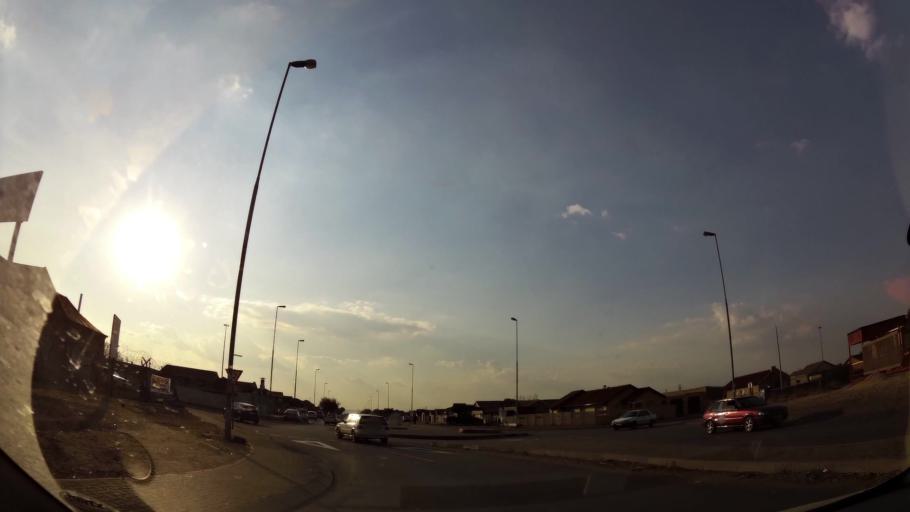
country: ZA
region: Gauteng
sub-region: Ekurhuleni Metropolitan Municipality
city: Germiston
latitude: -26.3482
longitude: 28.2191
